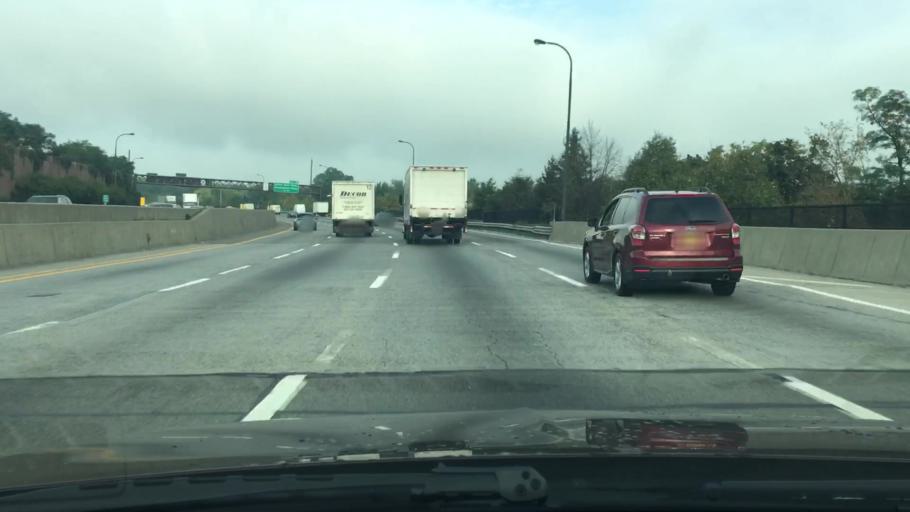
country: US
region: New York
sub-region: Nassau County
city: Lake Success
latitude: 40.7691
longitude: -73.7037
